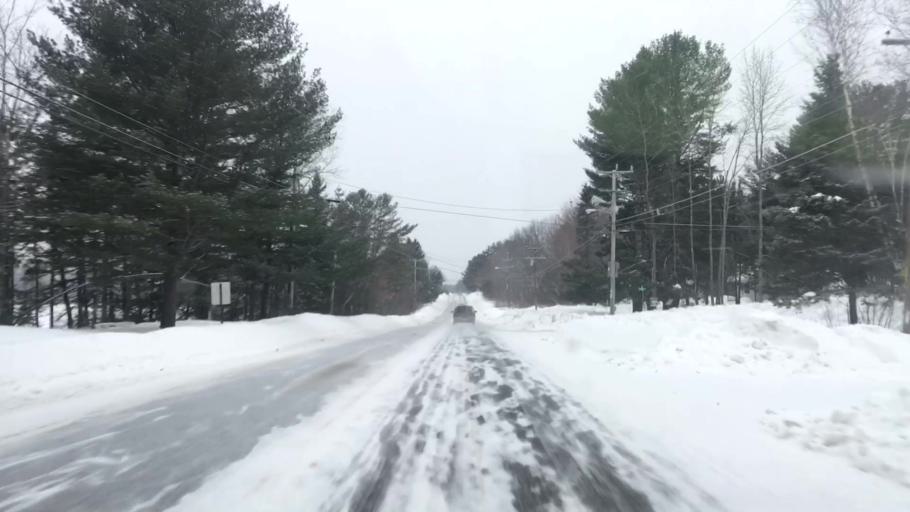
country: US
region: Maine
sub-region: Penobscot County
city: Medway
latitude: 45.5957
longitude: -68.4935
